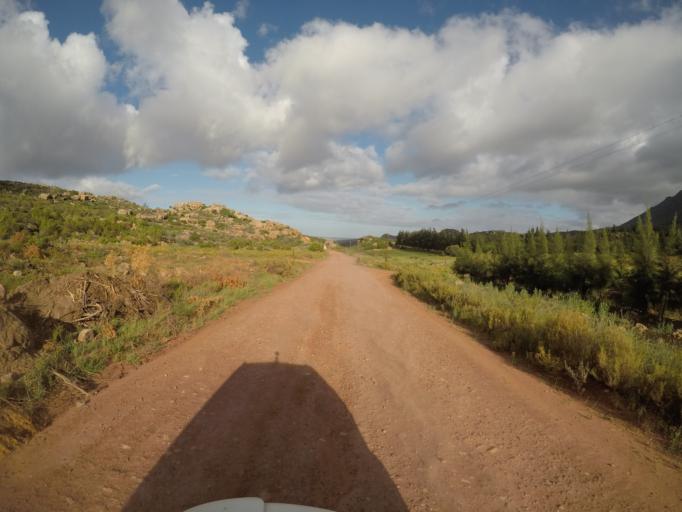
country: ZA
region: Western Cape
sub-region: West Coast District Municipality
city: Clanwilliam
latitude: -32.3401
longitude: 18.7650
